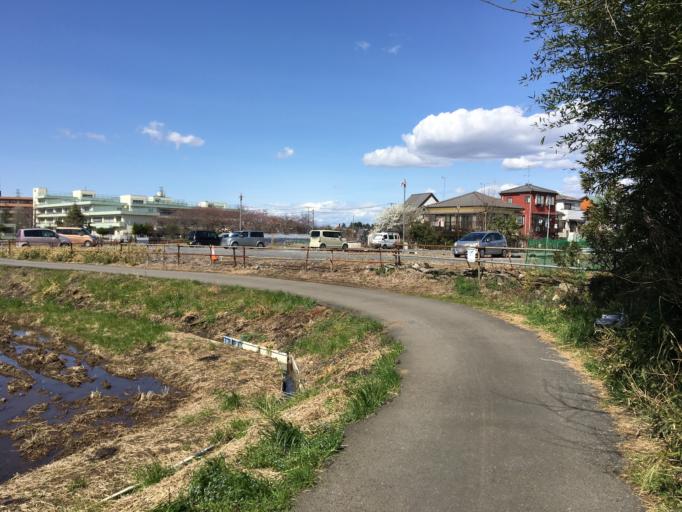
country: JP
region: Saitama
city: Shiki
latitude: 35.8370
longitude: 139.5714
